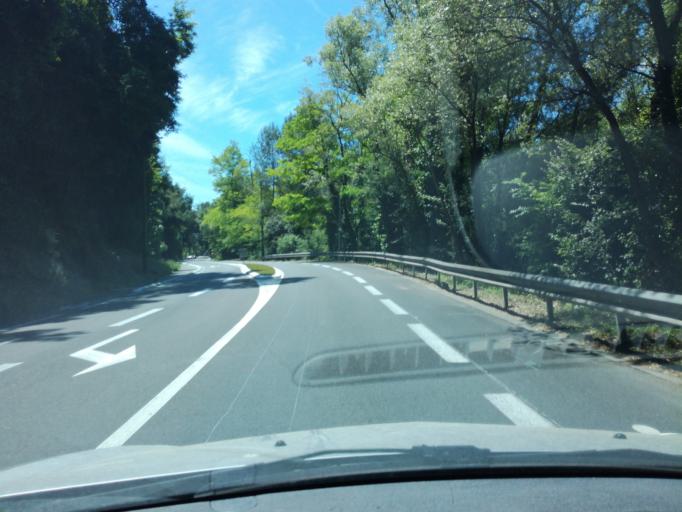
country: FR
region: Provence-Alpes-Cote d'Azur
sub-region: Departement des Alpes-Maritimes
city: Mougins
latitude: 43.5996
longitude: 7.0030
